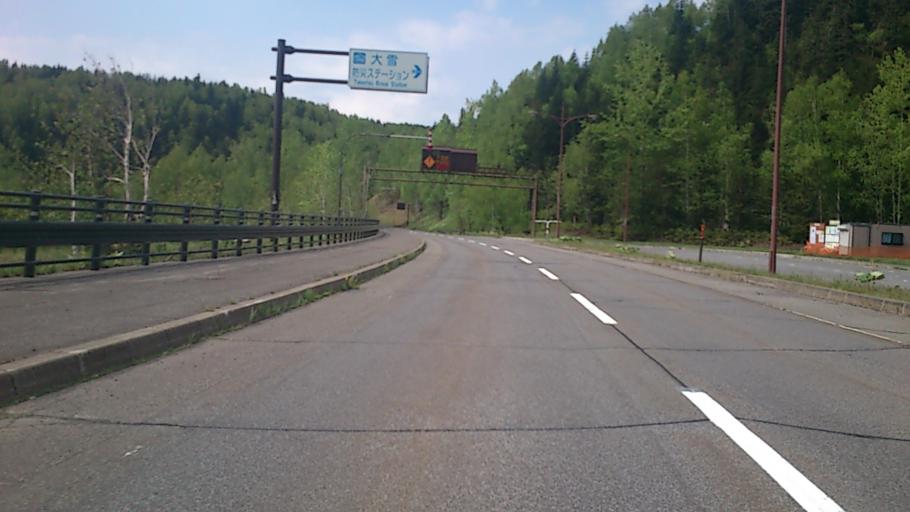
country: JP
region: Hokkaido
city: Kamikawa
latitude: 43.6654
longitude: 143.0364
